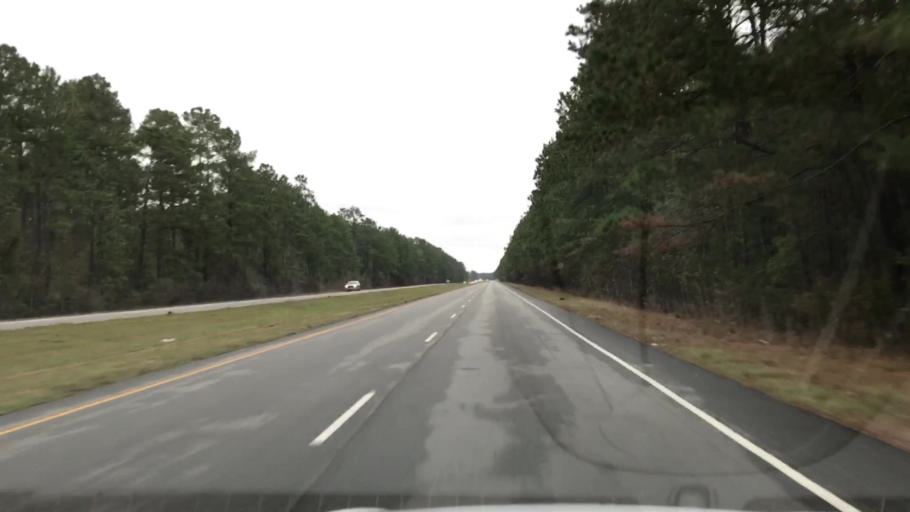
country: US
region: South Carolina
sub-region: Charleston County
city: Awendaw
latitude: 33.1612
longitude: -79.4257
